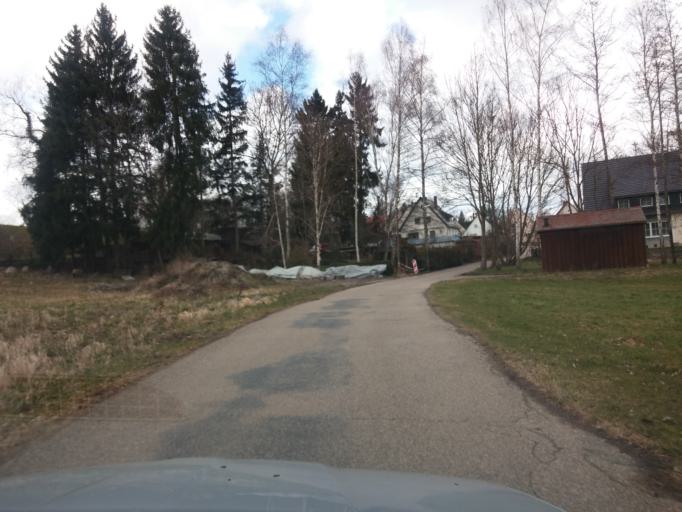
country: DE
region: Bavaria
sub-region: Swabia
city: Buxheim
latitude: 47.9766
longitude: 10.1480
